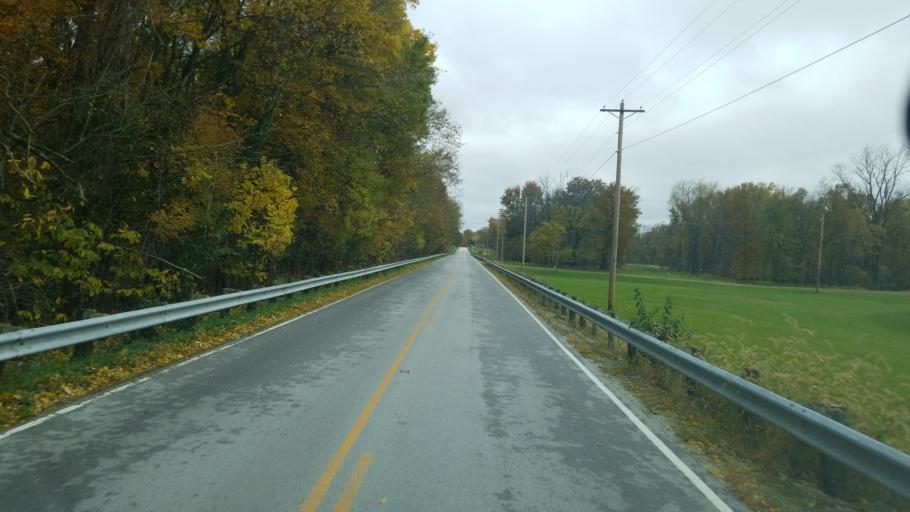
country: US
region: Ohio
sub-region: Sandusky County
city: Mount Carmel
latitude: 41.0665
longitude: -82.9464
